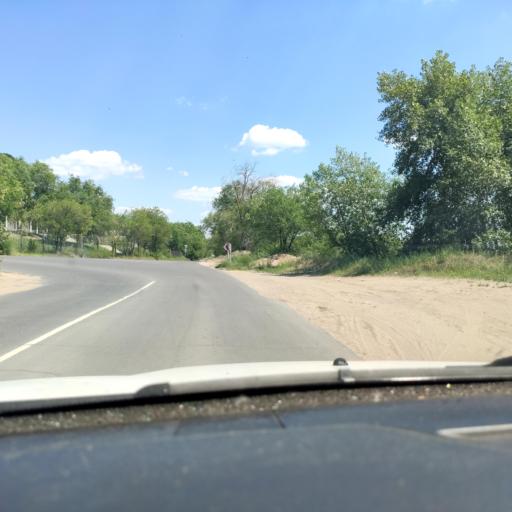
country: RU
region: Samara
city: Pribrezhnyy
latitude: 53.4833
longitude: 49.8462
